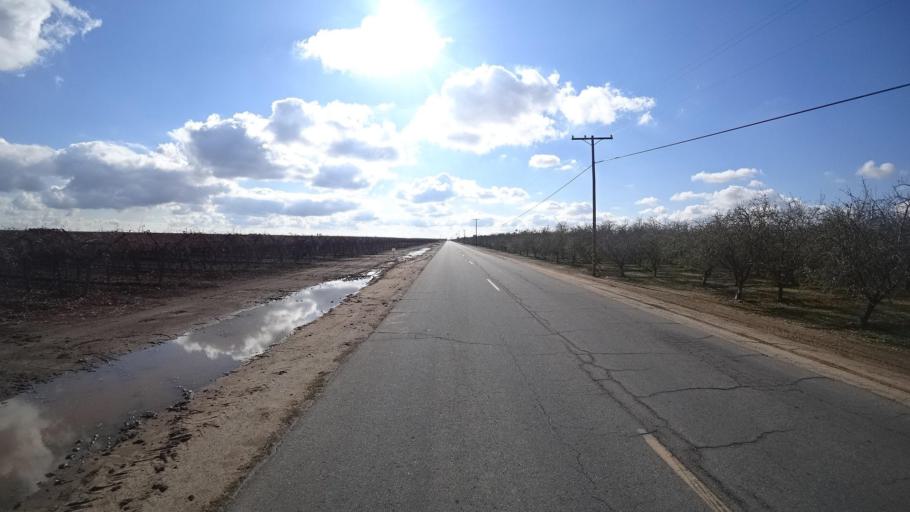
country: US
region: California
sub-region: Kern County
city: McFarland
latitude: 35.6724
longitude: -119.2048
